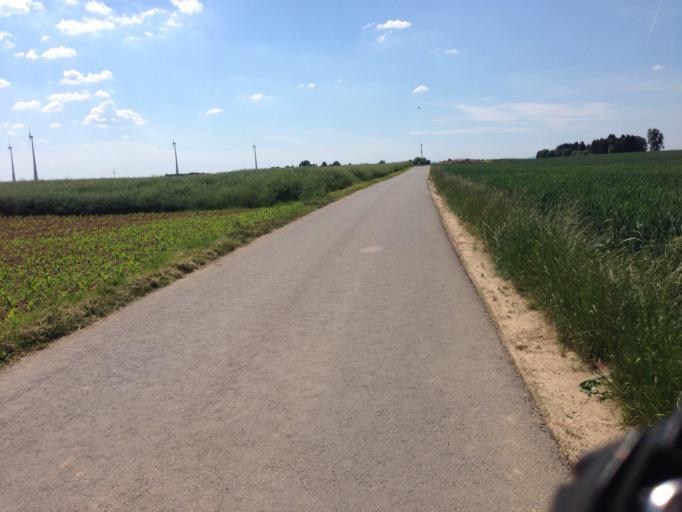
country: DE
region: Hesse
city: Bruchkobel
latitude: 50.2155
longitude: 8.9058
